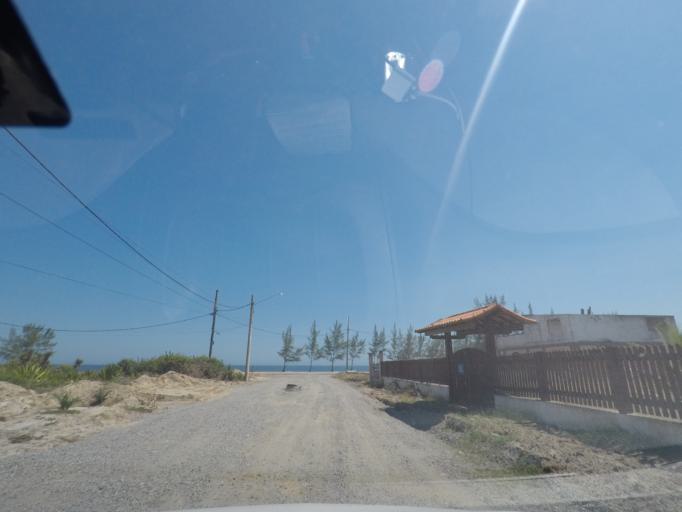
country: BR
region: Rio de Janeiro
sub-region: Marica
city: Marica
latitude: -22.9714
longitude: -42.9064
